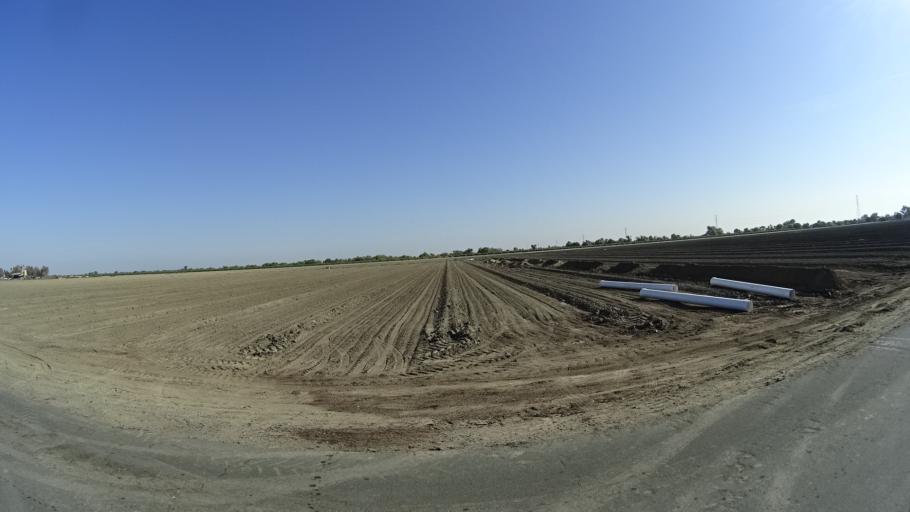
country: US
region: California
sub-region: Fresno County
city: Riverdale
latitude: 36.3766
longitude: -119.8966
